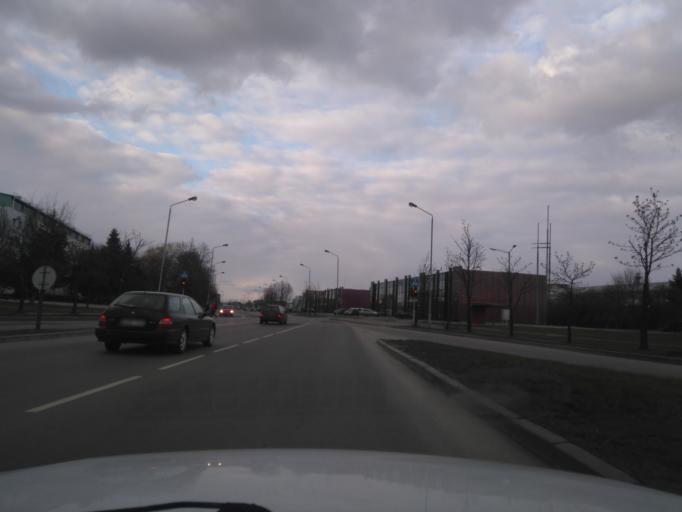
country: LT
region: Kauno apskritis
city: Dainava (Kaunas)
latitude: 54.9049
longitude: 23.9793
